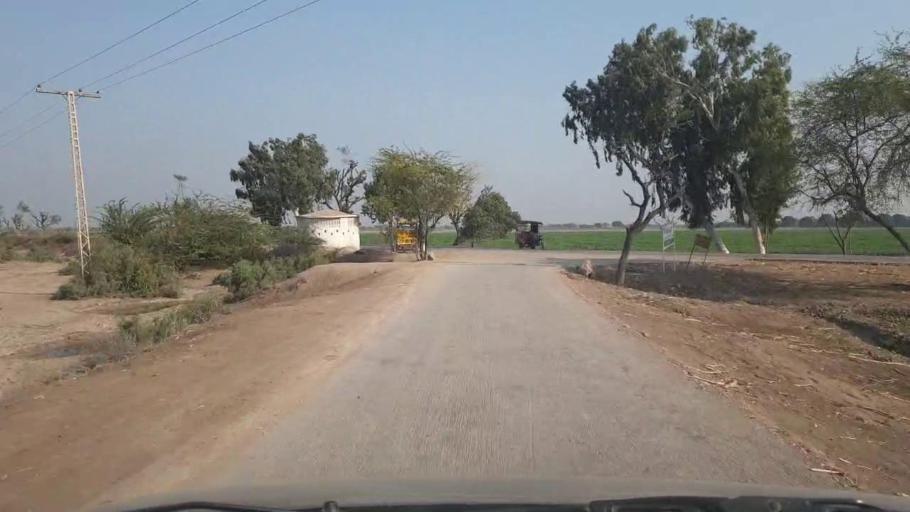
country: PK
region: Sindh
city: Digri
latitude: 25.2364
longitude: 69.1983
